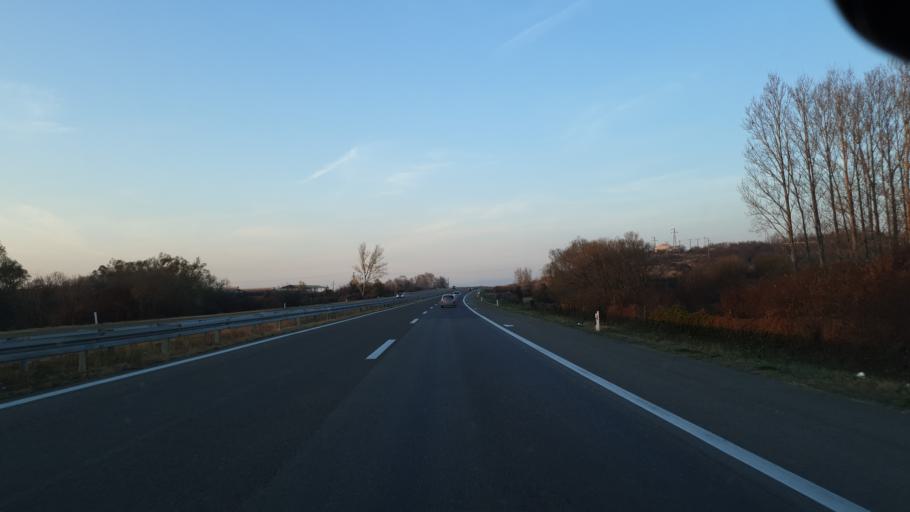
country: RS
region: Central Serbia
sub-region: Nisavski Okrug
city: Nis
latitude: 43.4007
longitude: 21.7957
